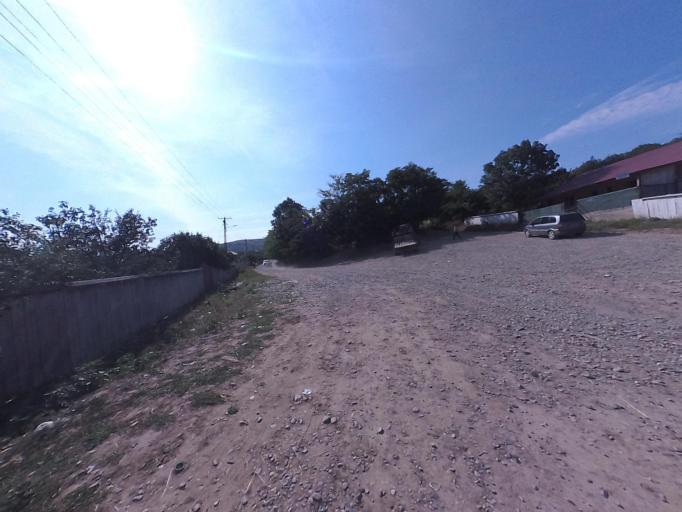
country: RO
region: Vaslui
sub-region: Comuna Osesti
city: Buda
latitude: 46.7598
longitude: 27.4258
